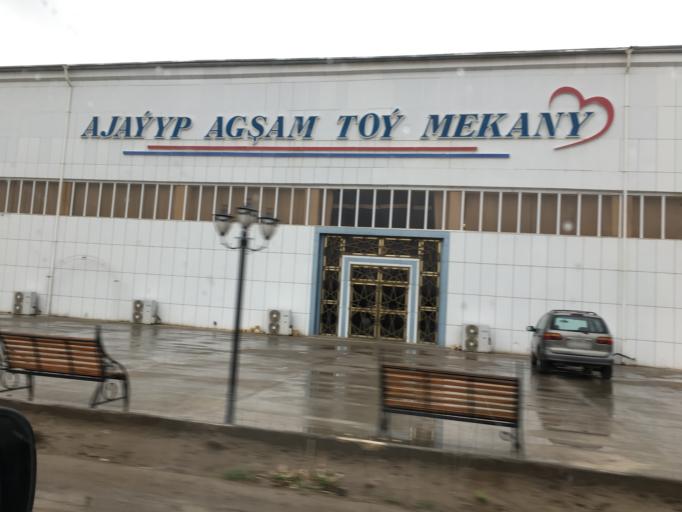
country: TM
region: Mary
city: Yoloeten
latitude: 37.2883
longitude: 62.3582
